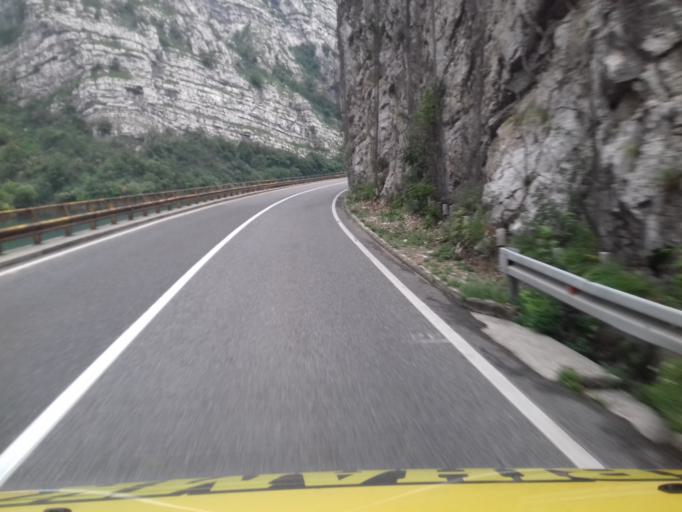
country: BA
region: Federation of Bosnia and Herzegovina
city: Jablanica
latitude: 43.6074
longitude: 17.7418
